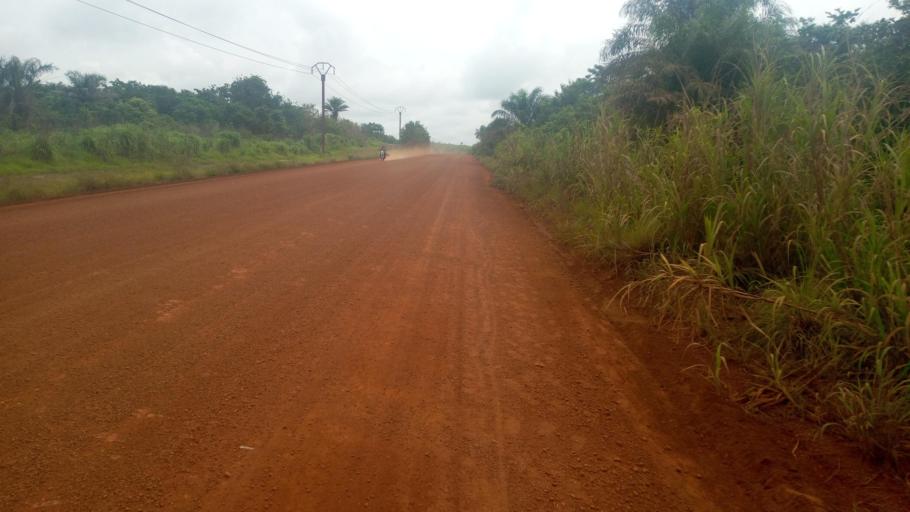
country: SL
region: Southern Province
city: Mogbwemo
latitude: 7.7165
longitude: -12.2853
